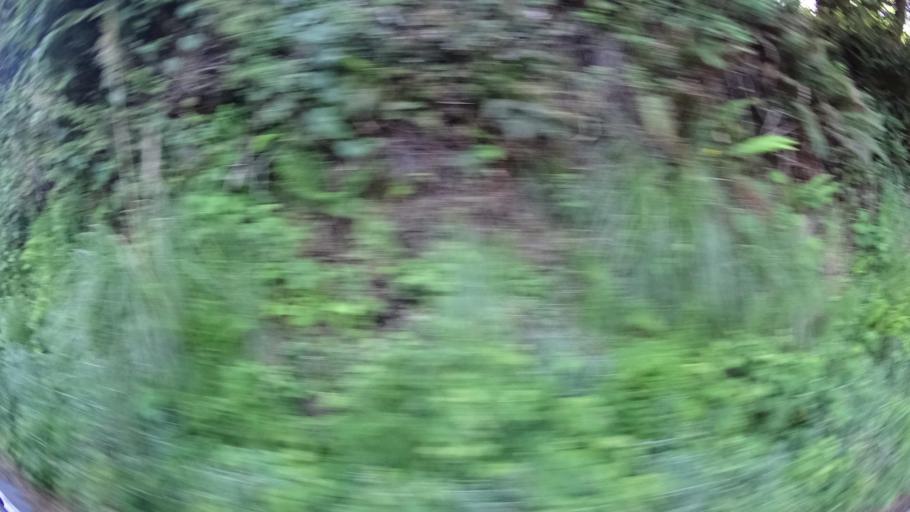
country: US
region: California
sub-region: Humboldt County
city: Westhaven-Moonstone
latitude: 41.1201
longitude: -124.1567
